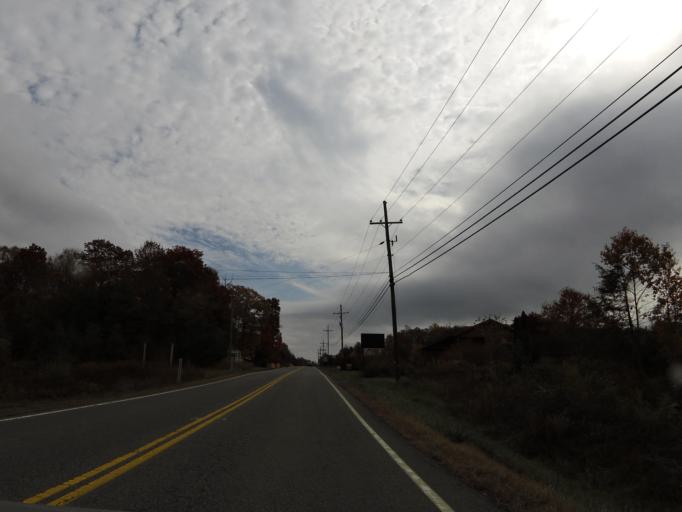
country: US
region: Virginia
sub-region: Carroll County
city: Cana
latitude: 36.6729
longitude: -80.6946
